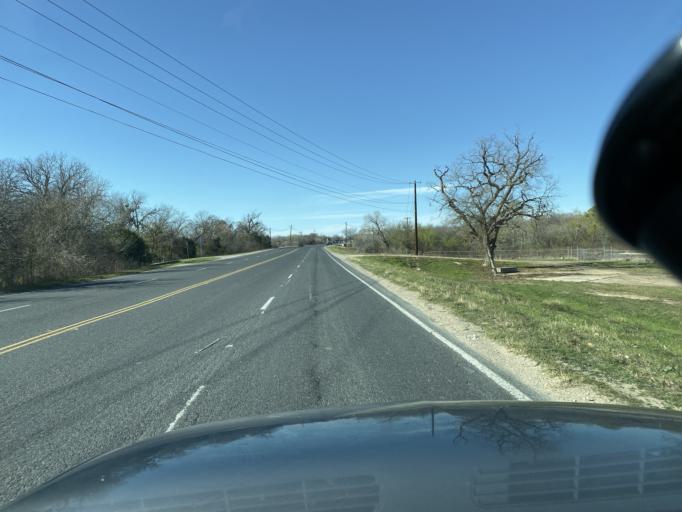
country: US
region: Texas
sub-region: Travis County
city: Garfield
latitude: 30.1704
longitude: -97.6636
